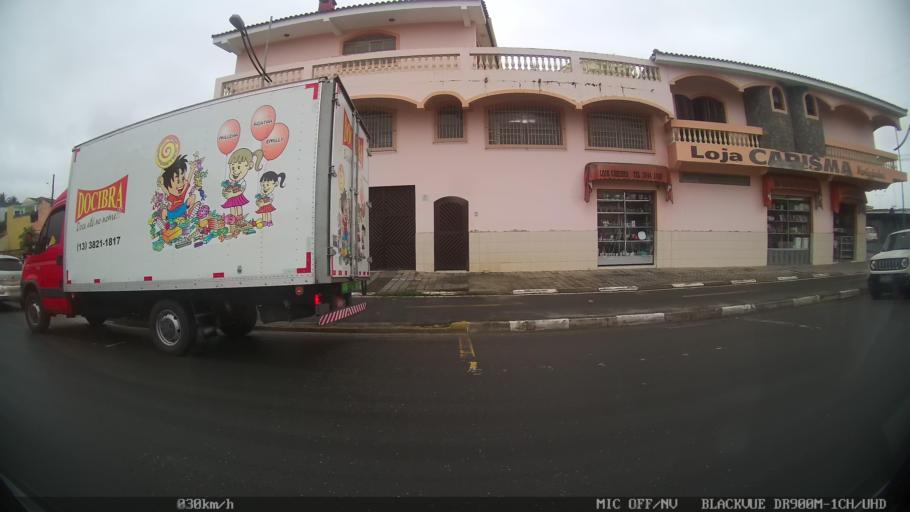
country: BR
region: Sao Paulo
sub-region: Juquia
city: Juquia
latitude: -24.3181
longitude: -47.6347
